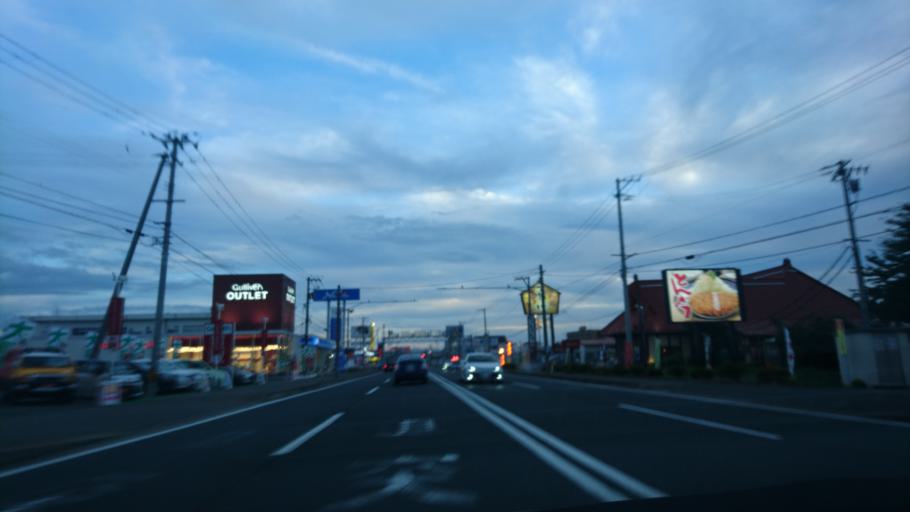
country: JP
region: Iwate
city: Morioka-shi
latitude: 39.6785
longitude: 141.1557
